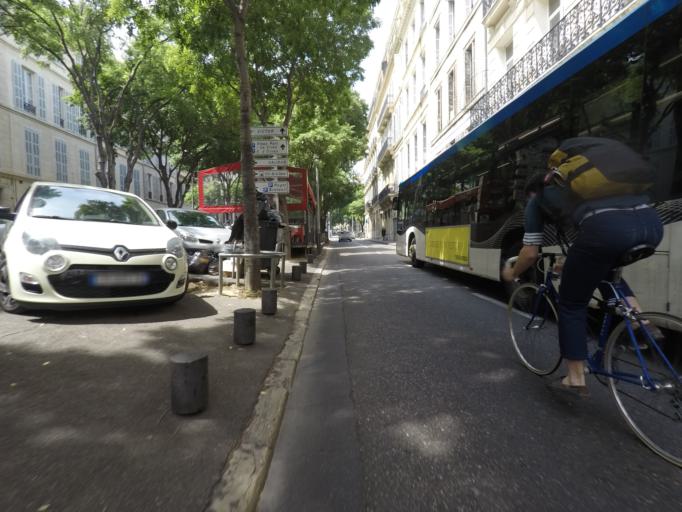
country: FR
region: Provence-Alpes-Cote d'Azur
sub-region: Departement des Bouches-du-Rhone
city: Marseille 06
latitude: 43.2905
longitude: 5.3771
